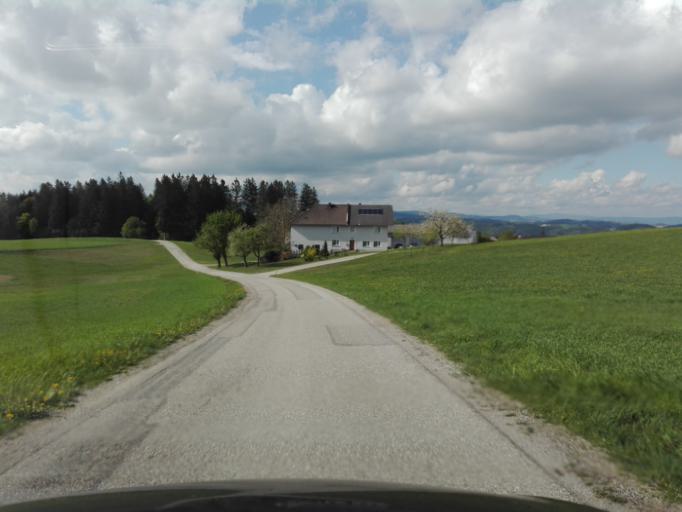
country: AT
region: Upper Austria
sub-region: Politischer Bezirk Rohrbach
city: Pfarrkirchen im Muehlkreis
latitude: 48.4109
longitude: 13.8588
